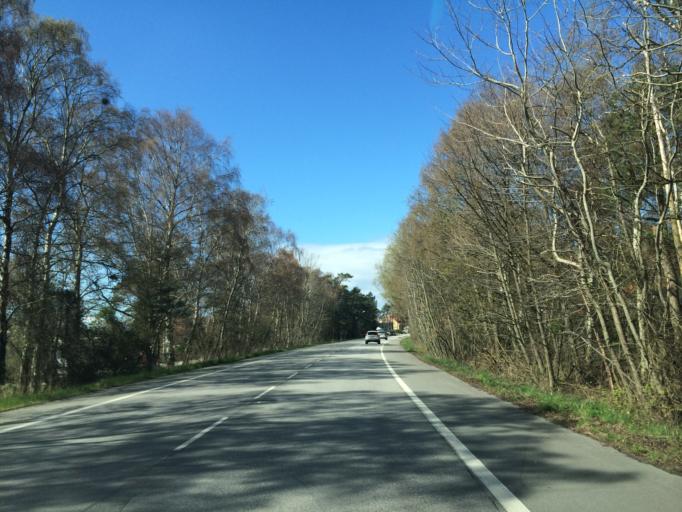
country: SE
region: Skane
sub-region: Vellinge Kommun
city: Skanor med Falsterbo
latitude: 55.4076
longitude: 12.8486
